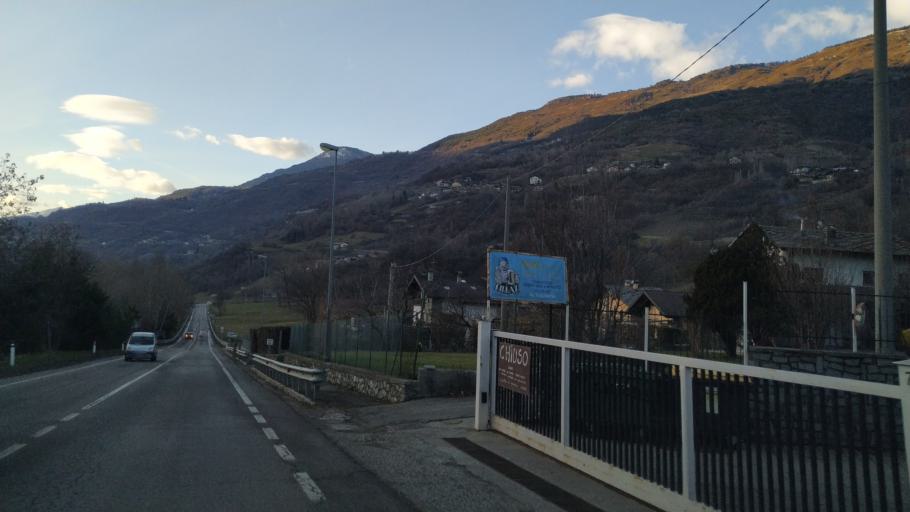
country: IT
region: Aosta Valley
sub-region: Valle d'Aosta
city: Chez Croiset
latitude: 45.7437
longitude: 7.5158
